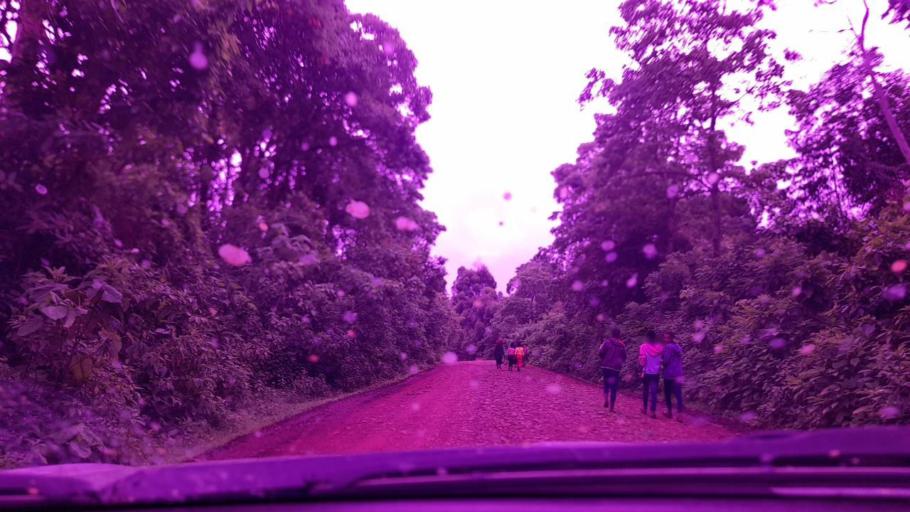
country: ET
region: Southern Nations, Nationalities, and People's Region
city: Tippi
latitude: 7.5727
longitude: 35.6438
